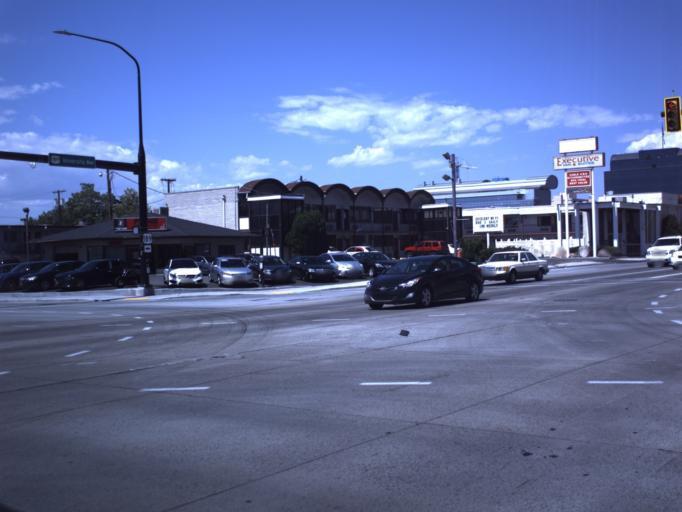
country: US
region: Utah
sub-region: Utah County
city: Provo
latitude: 40.2296
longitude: -111.6586
